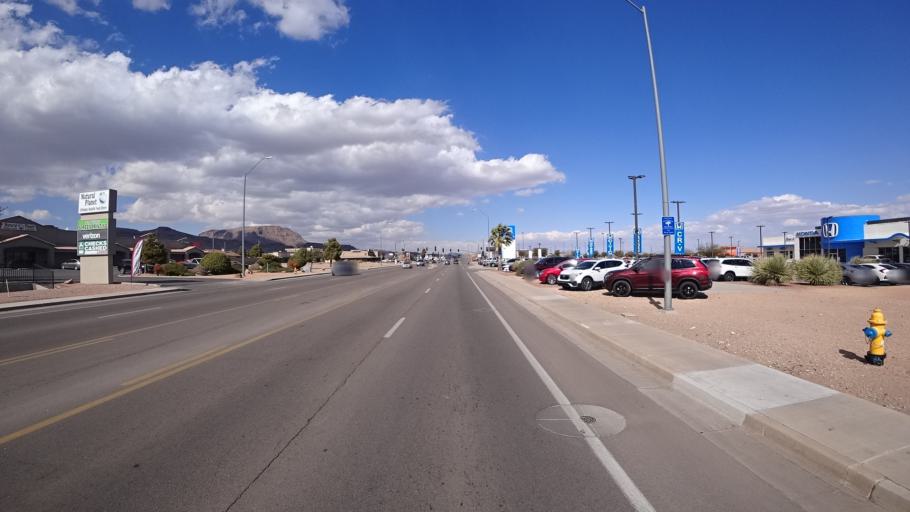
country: US
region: Arizona
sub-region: Mohave County
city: New Kingman-Butler
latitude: 35.2327
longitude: -114.0370
